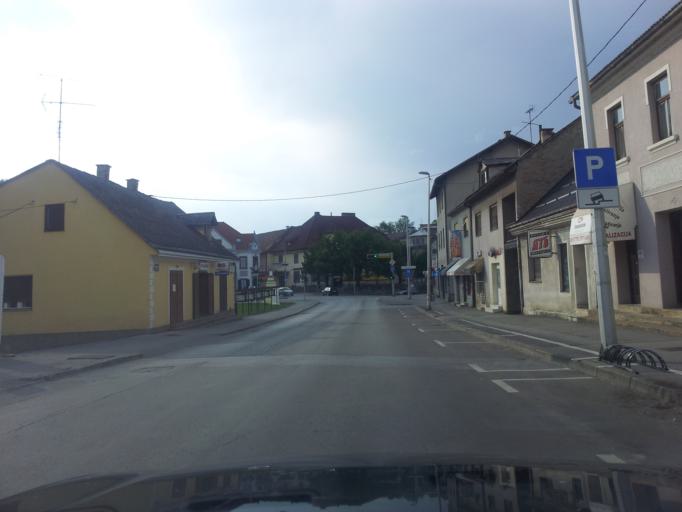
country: HR
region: Karlovacka
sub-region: Grad Karlovac
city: Karlovac
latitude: 45.4495
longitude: 15.5006
